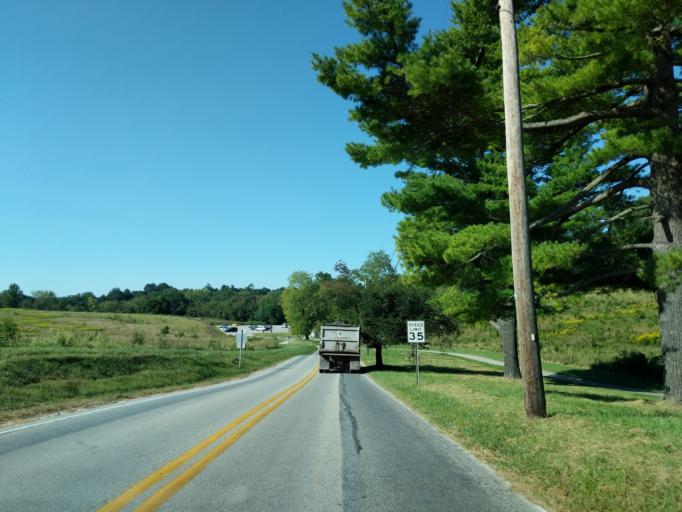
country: US
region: Pennsylvania
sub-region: Chester County
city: Chesterbrook
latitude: 40.0872
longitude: -75.4492
